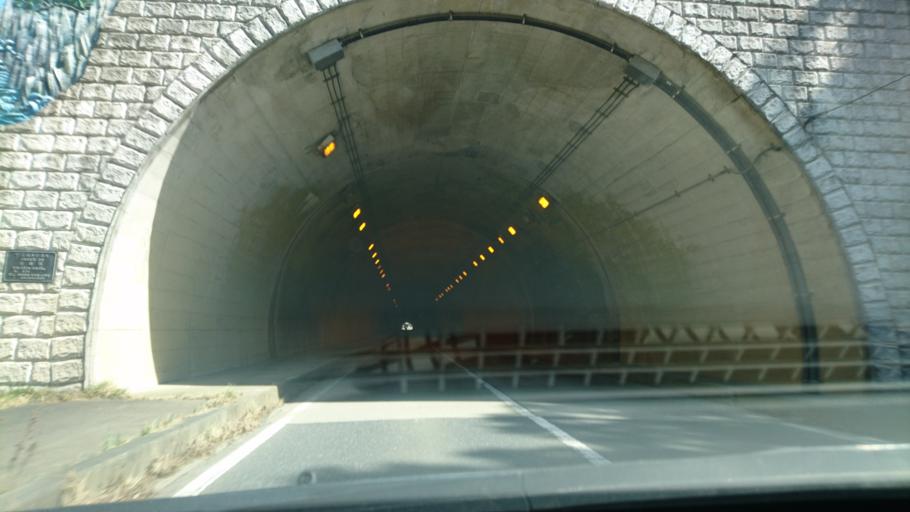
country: JP
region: Miyagi
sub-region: Oshika Gun
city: Onagawa Cho
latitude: 38.5866
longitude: 141.4776
